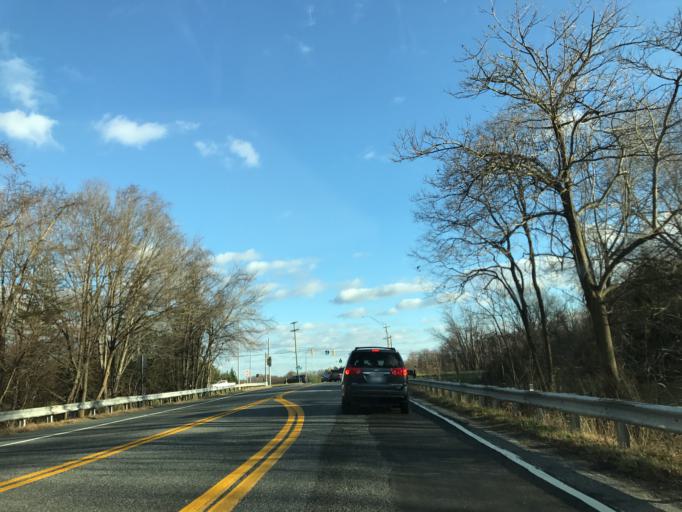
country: US
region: Maryland
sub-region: Harford County
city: Fallston
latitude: 39.5203
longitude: -76.4161
